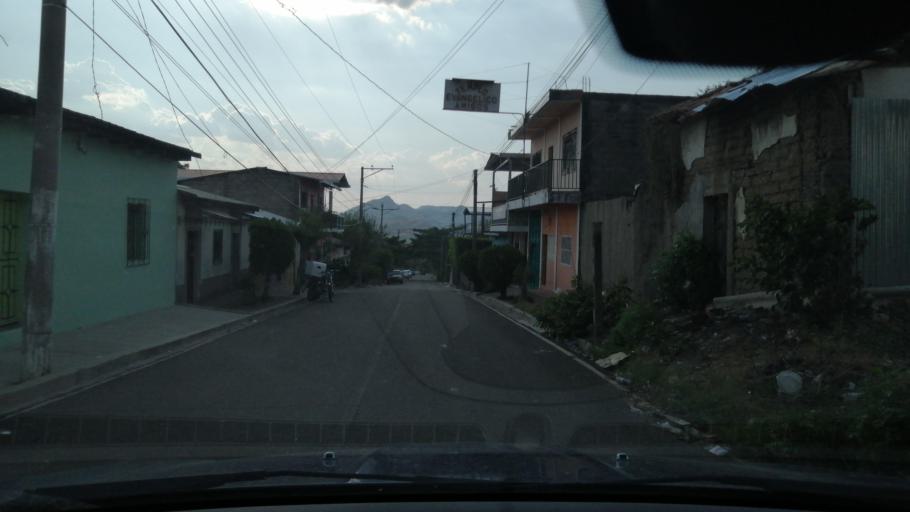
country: SV
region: Santa Ana
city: Metapan
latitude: 14.3325
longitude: -89.4366
